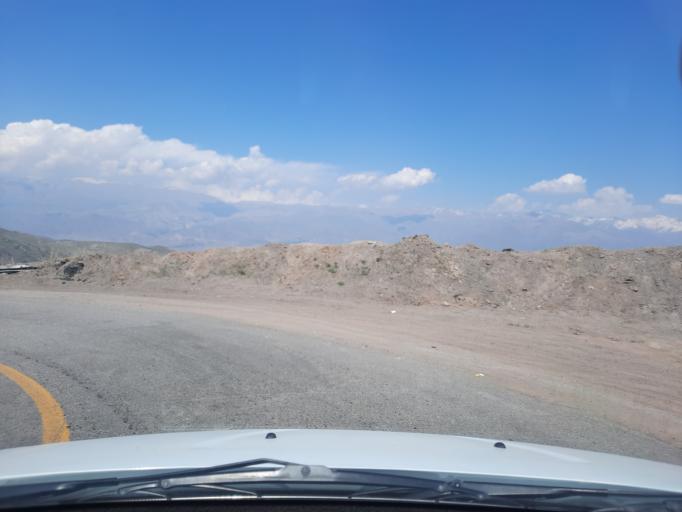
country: IR
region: Qazvin
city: Qazvin
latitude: 36.3957
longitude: 50.2167
